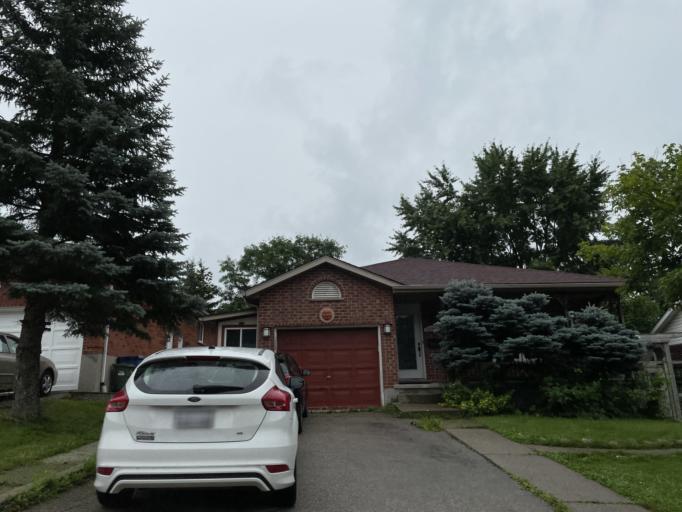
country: CA
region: Ontario
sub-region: Wellington County
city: Guelph
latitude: 43.5156
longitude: -80.2182
